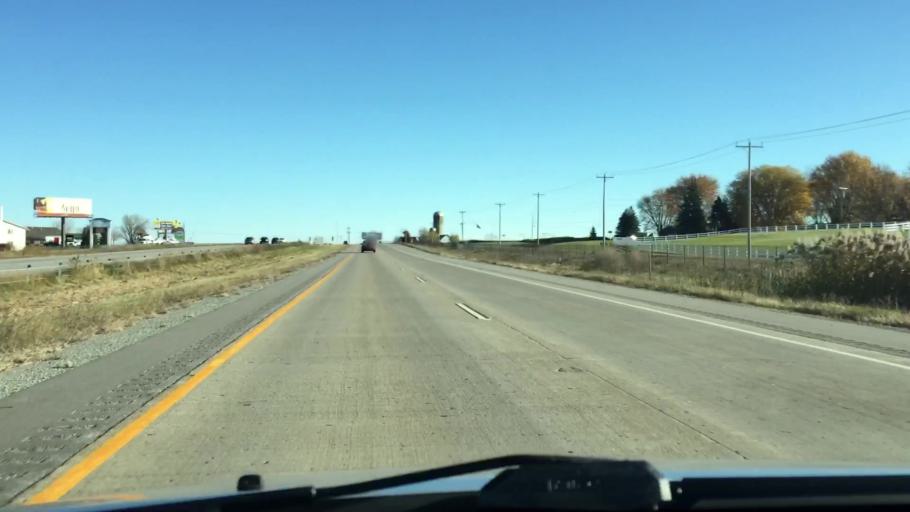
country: US
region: Wisconsin
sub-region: Brown County
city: Wrightstown
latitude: 44.3197
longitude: -88.2204
